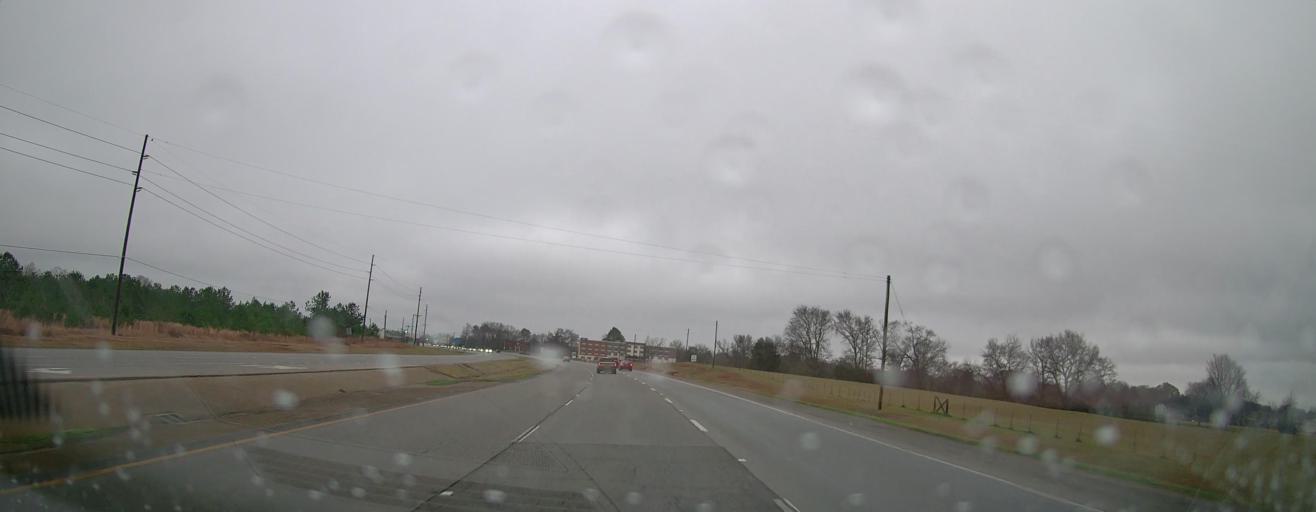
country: US
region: Alabama
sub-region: Morgan County
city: Decatur
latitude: 34.5954
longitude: -87.0315
